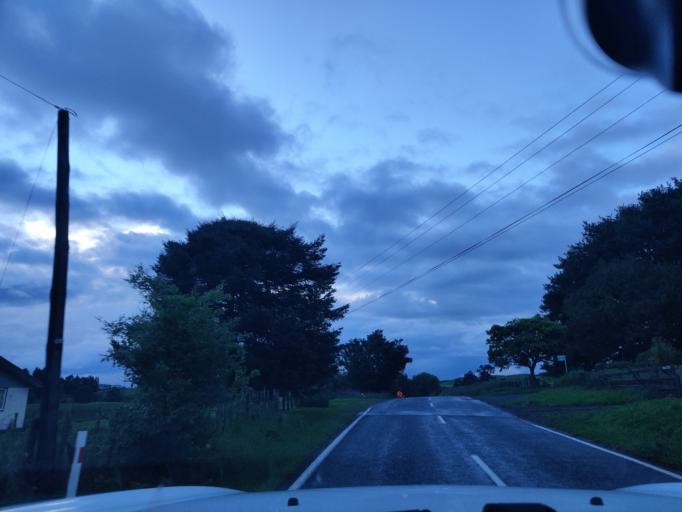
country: NZ
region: Waikato
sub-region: South Waikato District
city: Tokoroa
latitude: -38.1874
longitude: 175.7956
